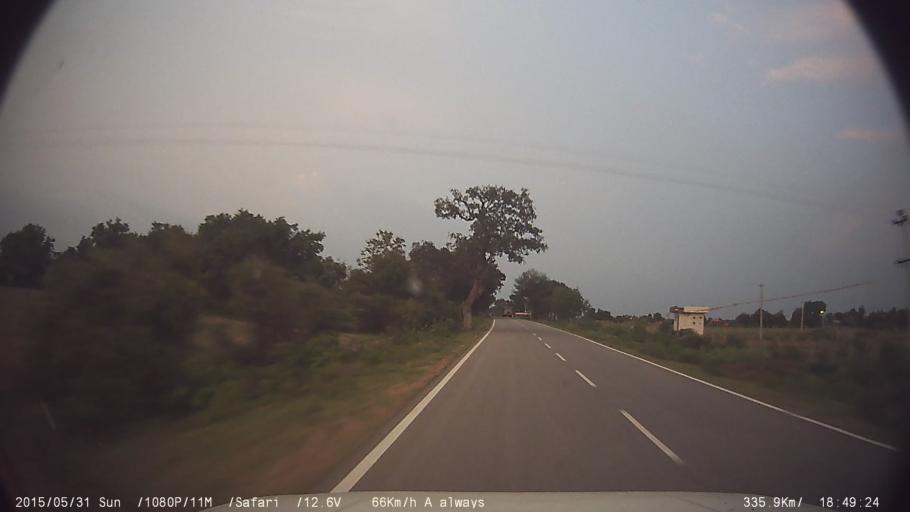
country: IN
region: Karnataka
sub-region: Mysore
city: Tirumakudal Narsipur
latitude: 12.1733
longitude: 76.8504
